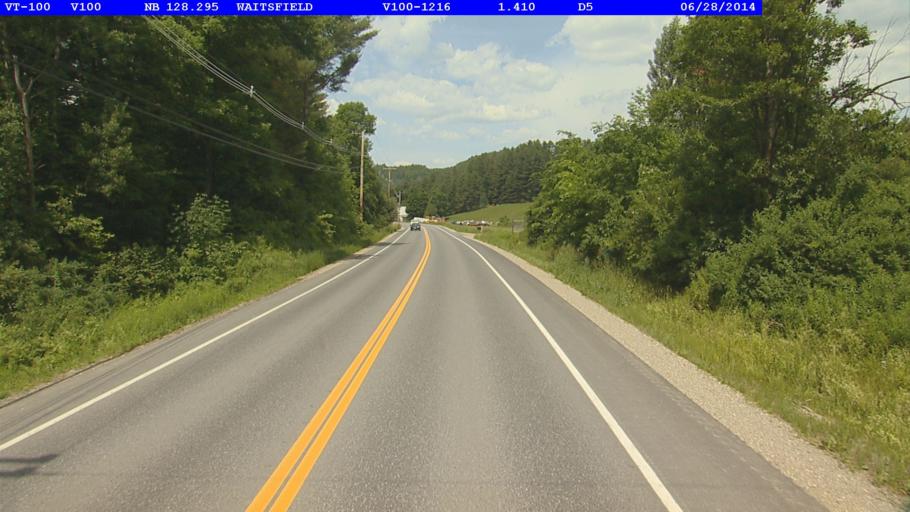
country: US
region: Vermont
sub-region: Washington County
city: Northfield
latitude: 44.1658
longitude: -72.8319
